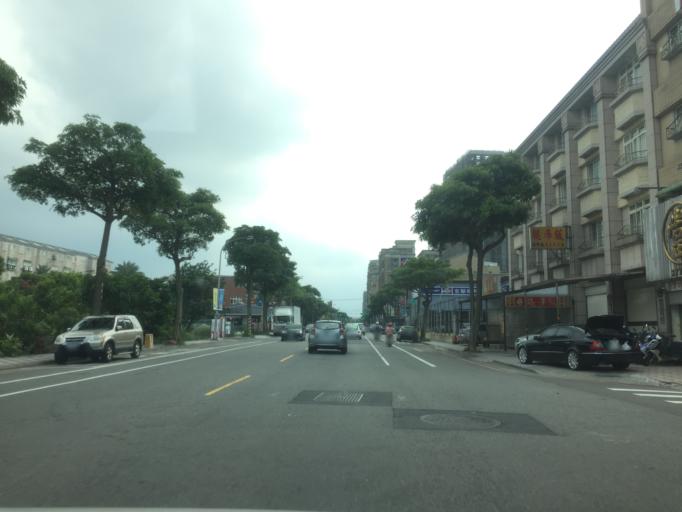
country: TW
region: Taiwan
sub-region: Taoyuan
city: Taoyuan
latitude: 24.9665
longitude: 121.3068
